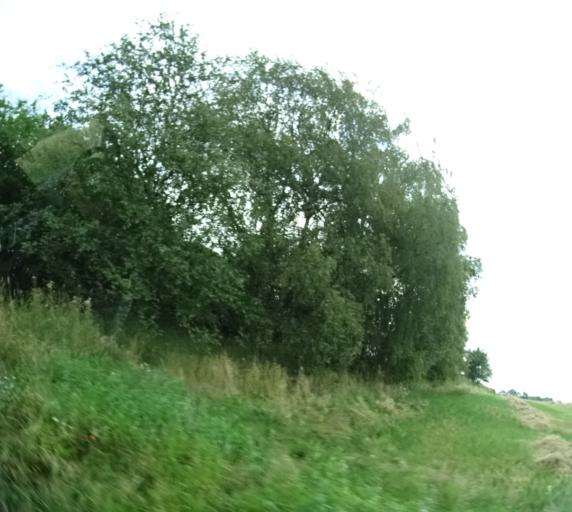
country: DK
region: Central Jutland
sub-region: Syddjurs Kommune
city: Ryomgard
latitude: 56.3984
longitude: 10.4869
